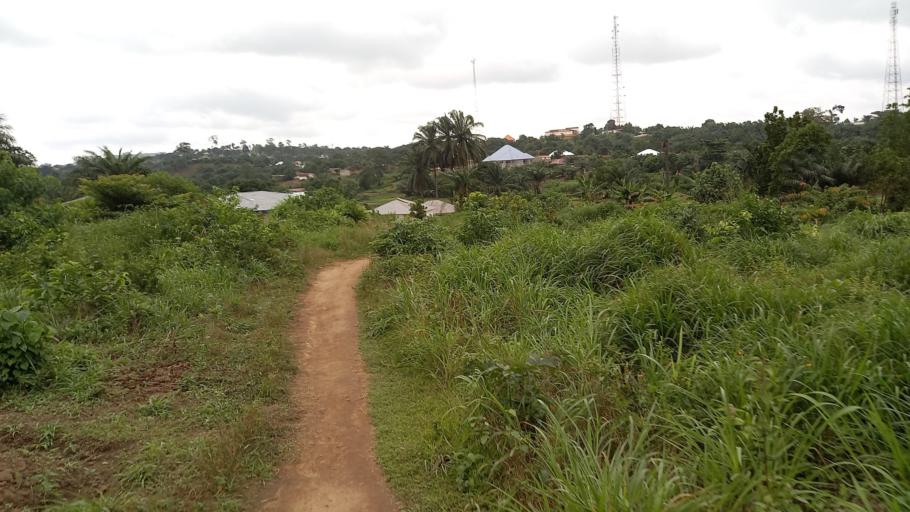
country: SL
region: Eastern Province
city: Kailahun
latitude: 8.2890
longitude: -10.5700
